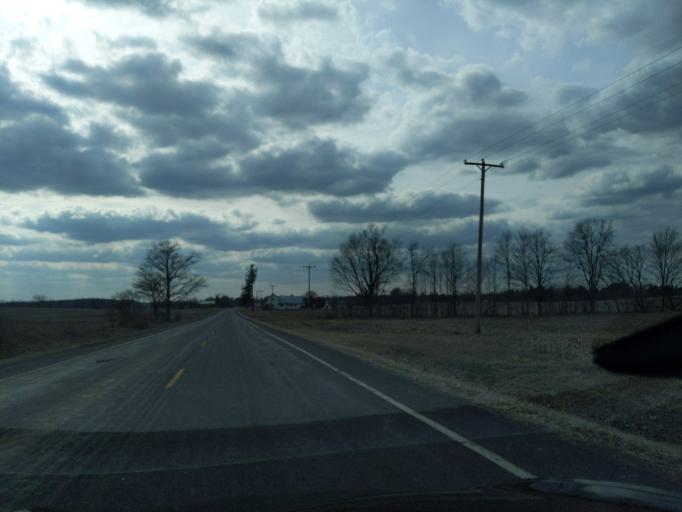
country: US
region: Michigan
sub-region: Ingham County
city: Mason
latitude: 42.5241
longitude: -84.4760
